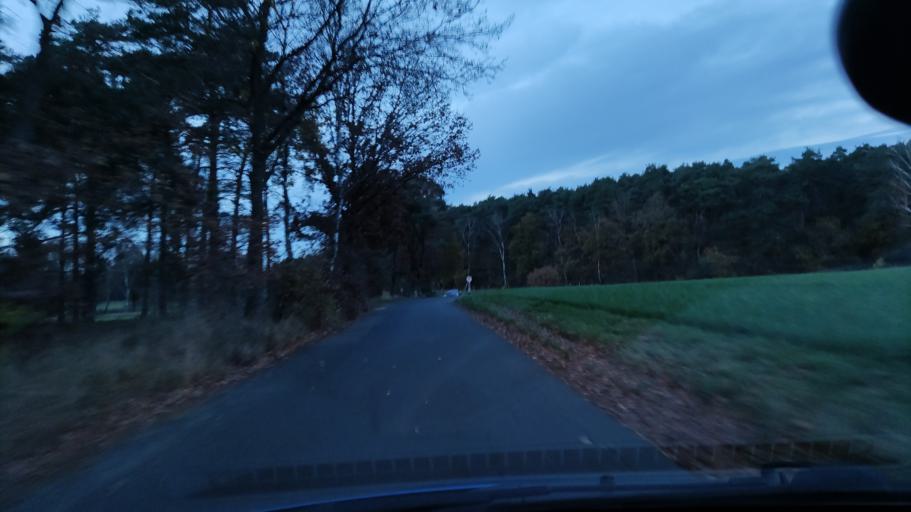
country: DE
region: Lower Saxony
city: Egestorf
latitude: 53.1519
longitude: 10.0319
